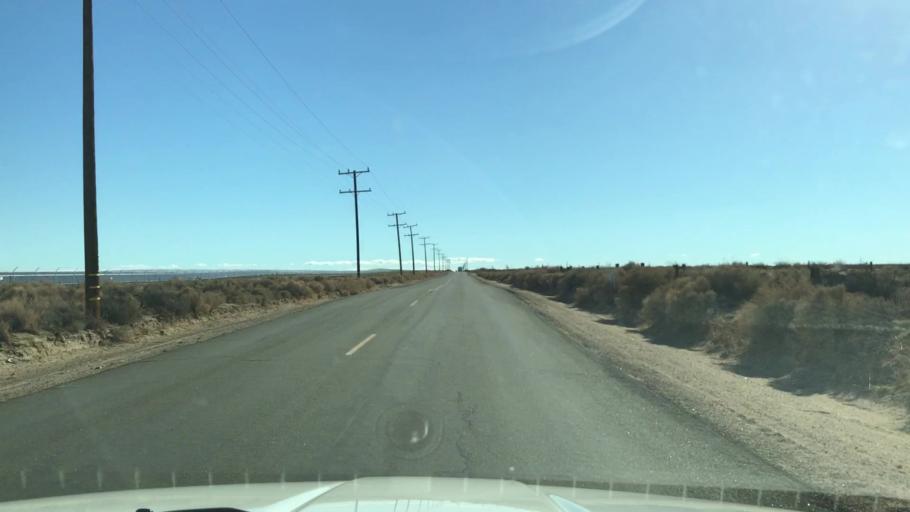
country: US
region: California
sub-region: Kern County
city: California City
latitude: 35.2503
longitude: -117.9859
